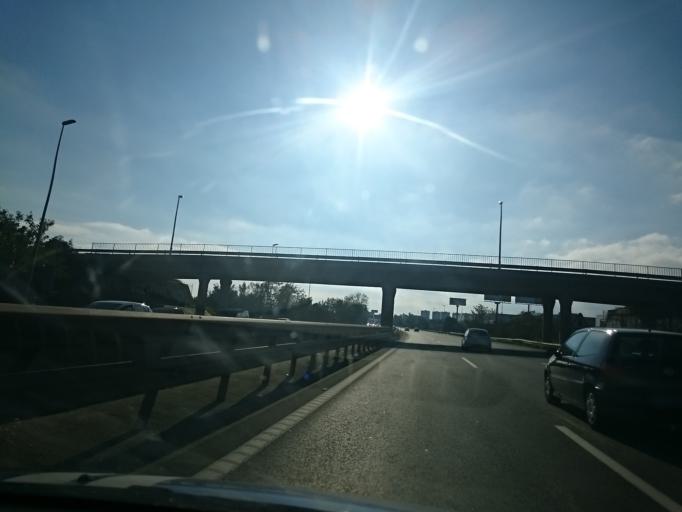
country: ES
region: Catalonia
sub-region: Provincia de Barcelona
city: Sant Boi de Llobregat
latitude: 41.3200
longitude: 2.0392
